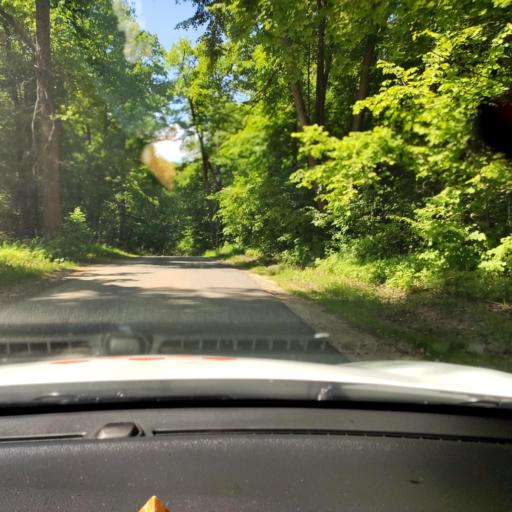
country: RU
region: Tatarstan
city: Osinovo
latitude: 55.7782
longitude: 48.7951
